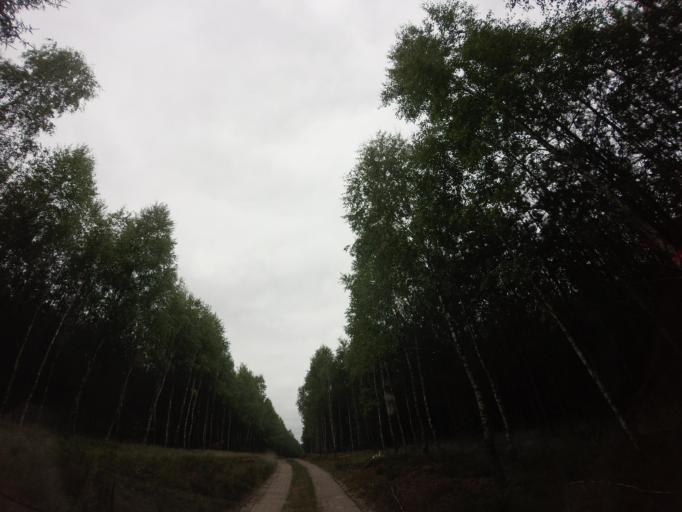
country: PL
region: West Pomeranian Voivodeship
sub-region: Powiat choszczenski
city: Drawno
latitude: 53.1399
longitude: 15.7380
